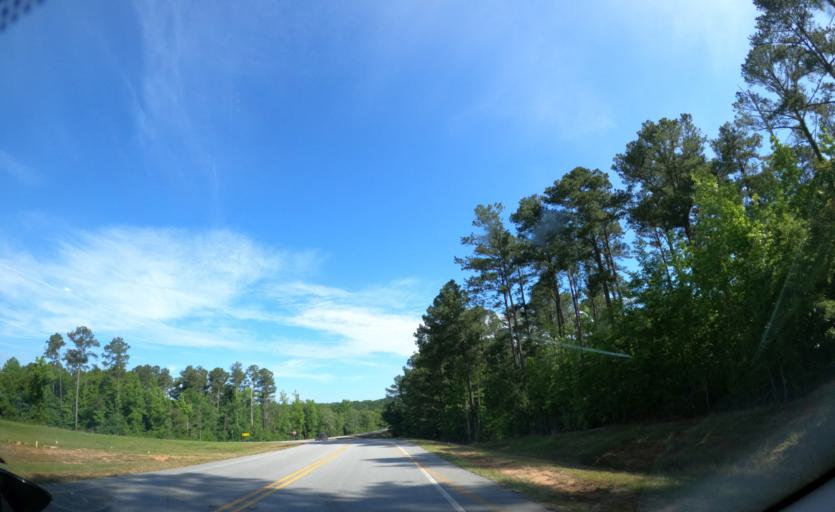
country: US
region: Georgia
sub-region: Lincoln County
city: Lincolnton
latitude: 33.8284
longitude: -82.4712
